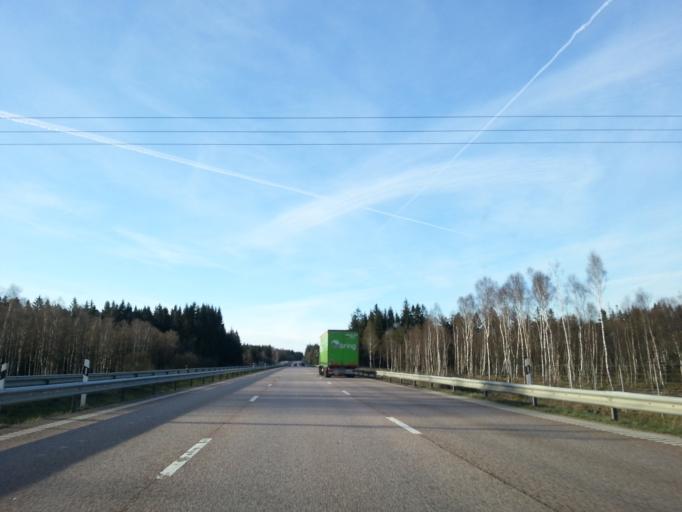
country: SE
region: Skane
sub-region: Bastads Kommun
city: Bastad
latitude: 56.3614
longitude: 12.9354
